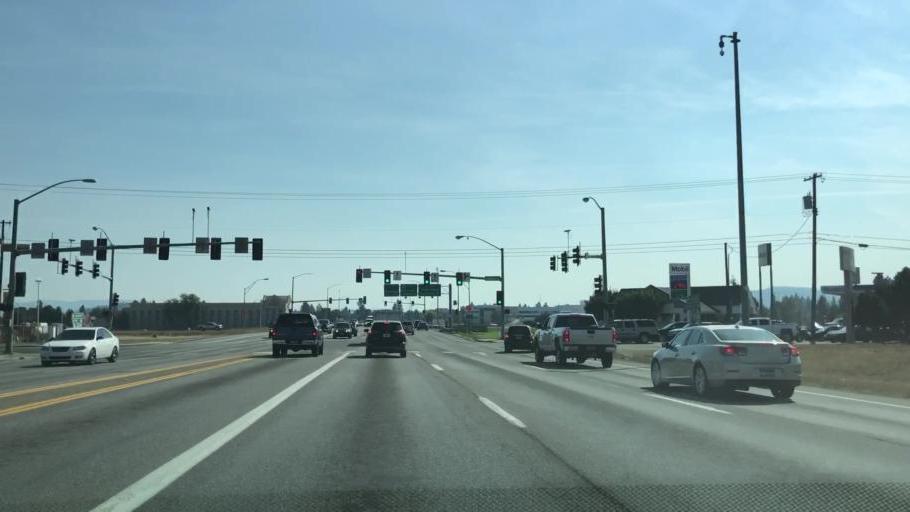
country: US
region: Idaho
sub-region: Kootenai County
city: Coeur d'Alene
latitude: 47.7014
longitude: -116.7917
